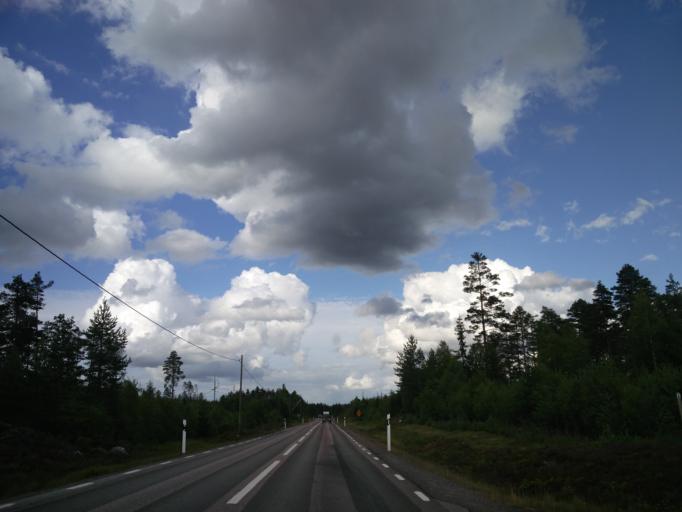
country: SE
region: Vaermland
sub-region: Torsby Kommun
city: Torsby
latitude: 60.3037
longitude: 13.0896
